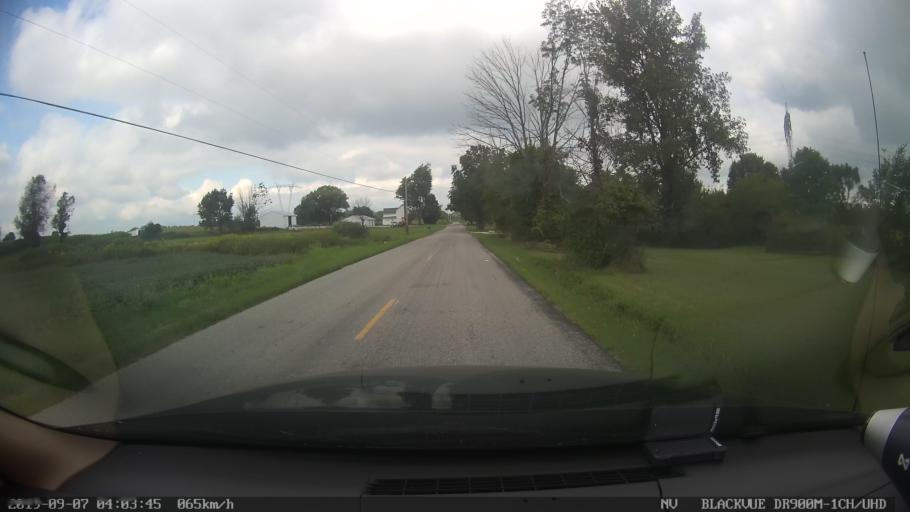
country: US
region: Ohio
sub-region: Licking County
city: Johnstown
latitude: 40.1884
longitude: -82.5940
